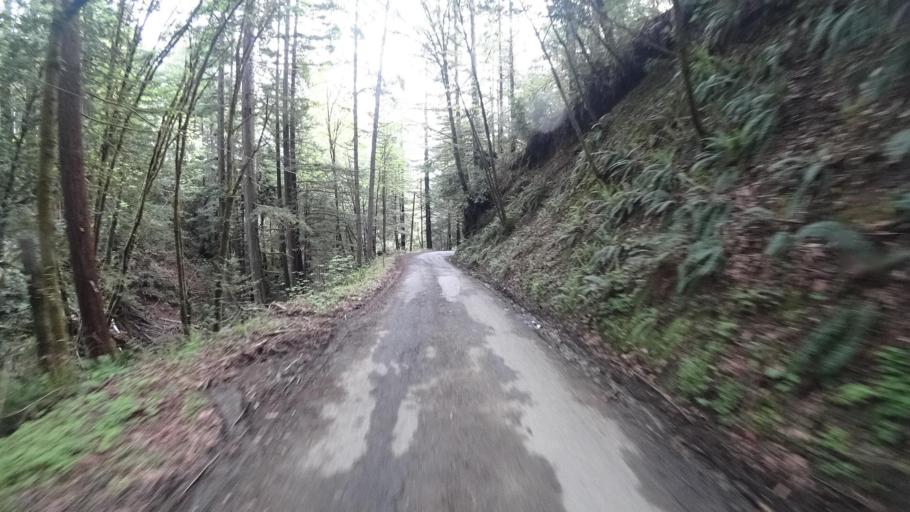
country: US
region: California
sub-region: Humboldt County
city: Redway
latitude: 40.3353
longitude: -123.9057
